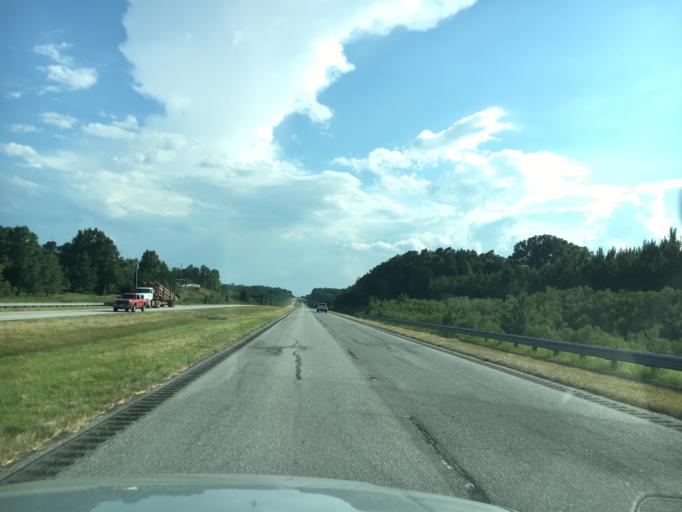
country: US
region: South Carolina
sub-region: Laurens County
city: Laurens
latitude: 34.3366
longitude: -81.9829
